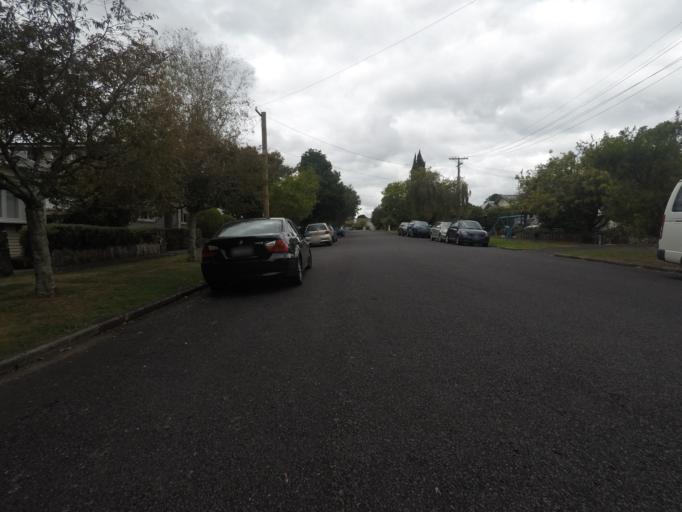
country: NZ
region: Auckland
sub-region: Auckland
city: Auckland
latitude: -36.8739
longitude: 174.7197
